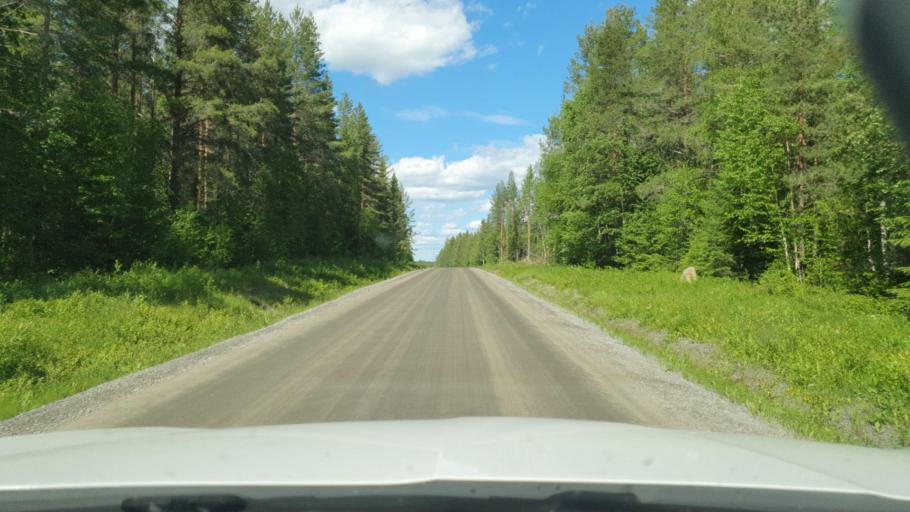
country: SE
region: Vaesterbotten
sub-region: Skelleftea Kommun
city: Forsbacka
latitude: 64.7741
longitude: 20.5167
